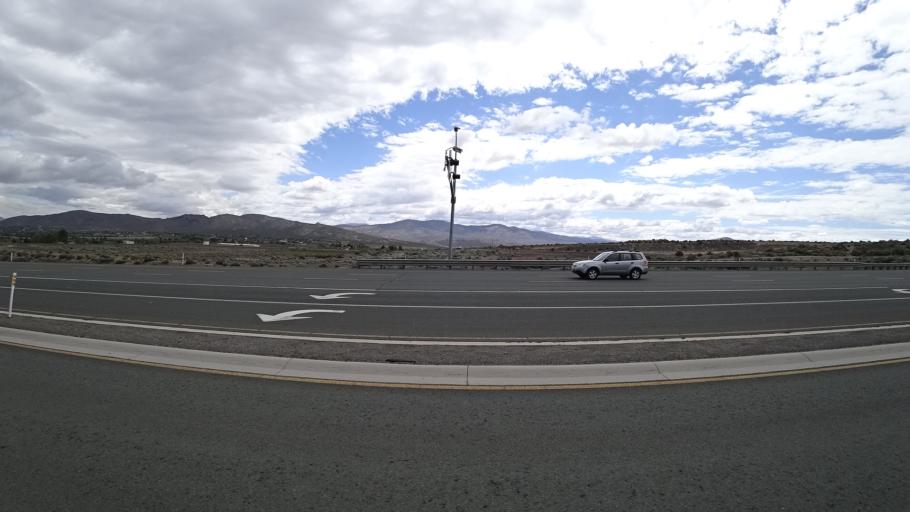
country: US
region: Nevada
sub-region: Douglas County
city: Indian Hills
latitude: 39.1086
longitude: -119.7741
